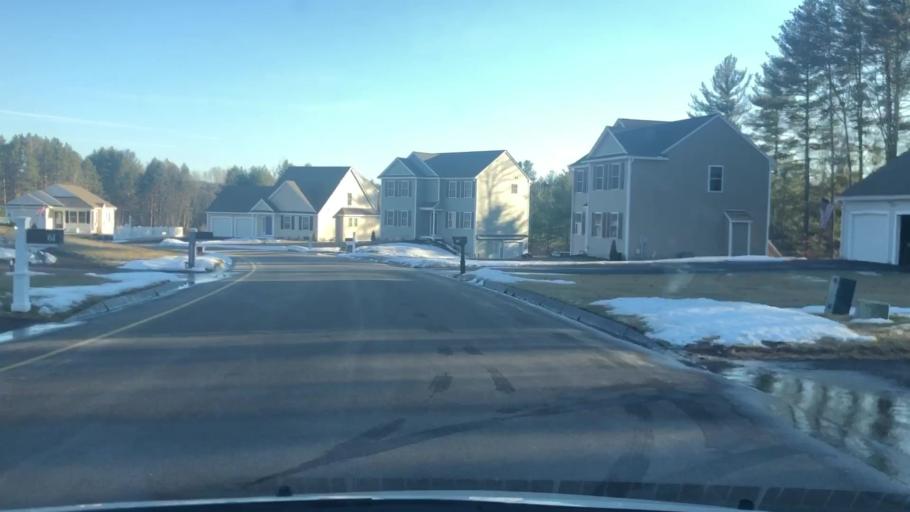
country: US
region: New Hampshire
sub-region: Hillsborough County
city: Milford
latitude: 42.8275
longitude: -71.6651
